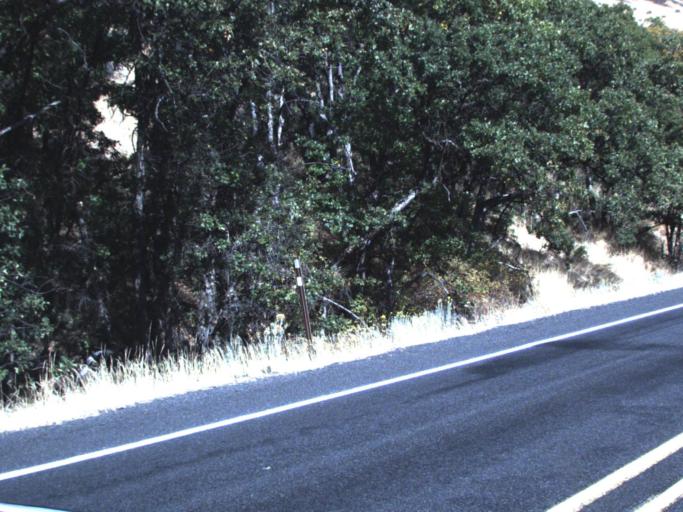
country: US
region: Washington
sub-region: Yakima County
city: Tieton
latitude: 46.7205
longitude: -120.8483
